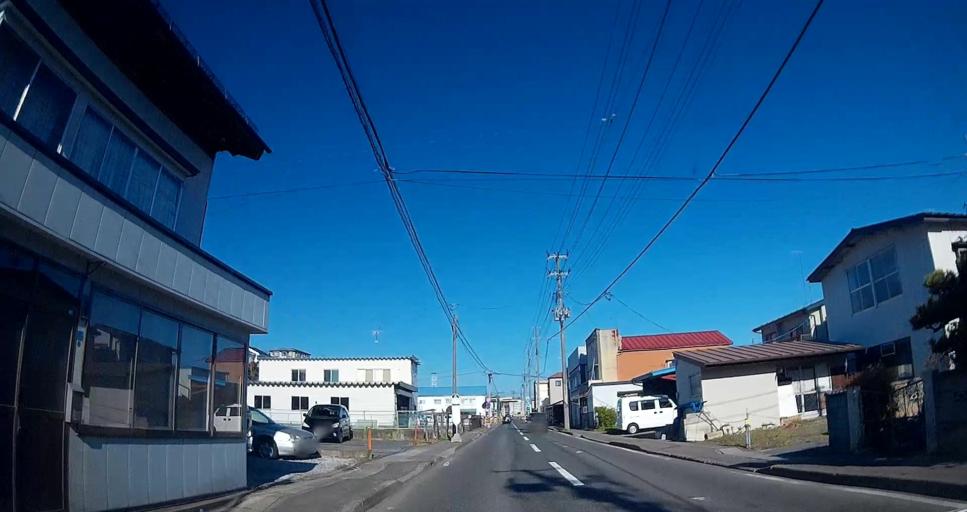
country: JP
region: Aomori
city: Hachinohe
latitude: 40.5235
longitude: 141.5333
